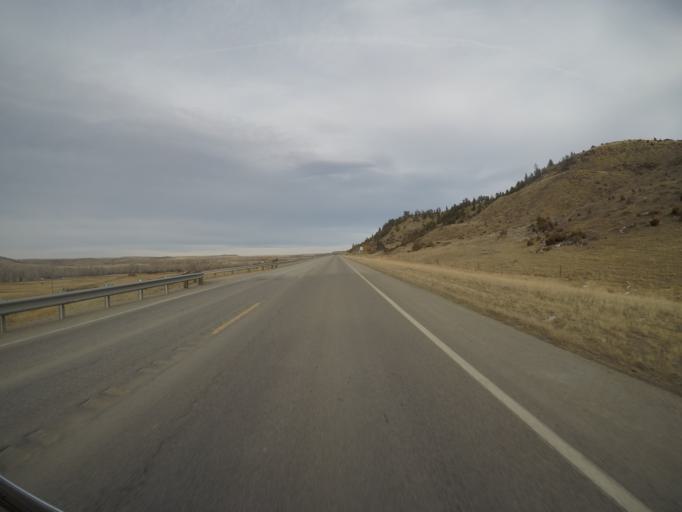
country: US
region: Montana
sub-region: Stillwater County
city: Absarokee
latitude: 45.5254
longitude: -109.4332
